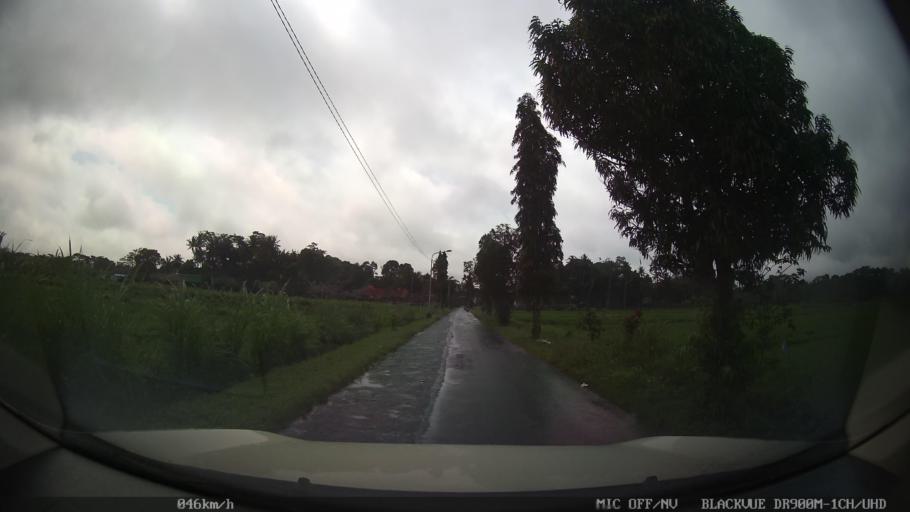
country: ID
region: Bali
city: Pegongan
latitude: -8.4948
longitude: 115.2259
